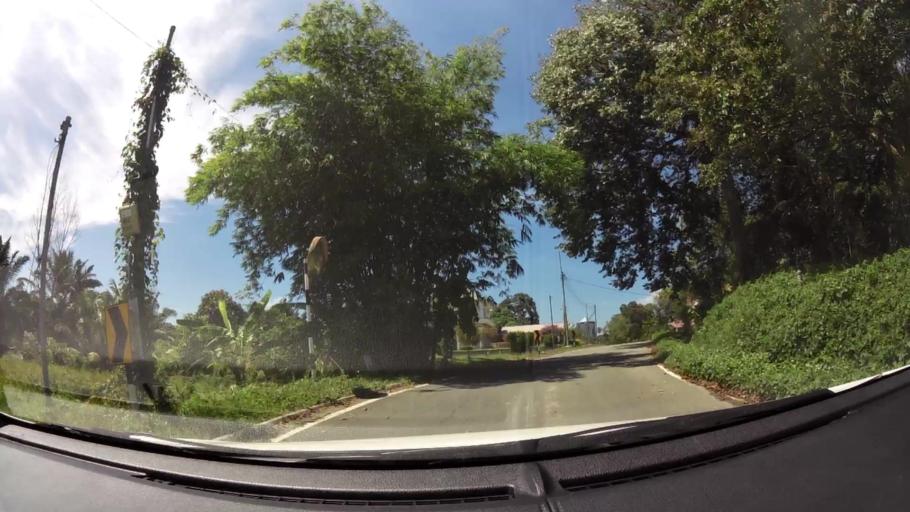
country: BN
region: Brunei and Muara
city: Bandar Seri Begawan
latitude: 4.9351
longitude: 114.9509
